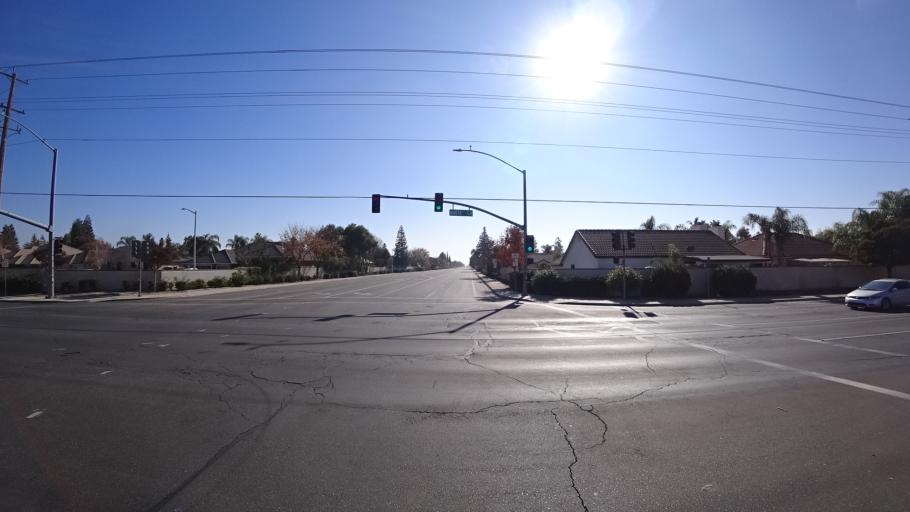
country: US
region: California
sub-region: Kern County
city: Greenacres
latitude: 35.3252
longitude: -119.1187
